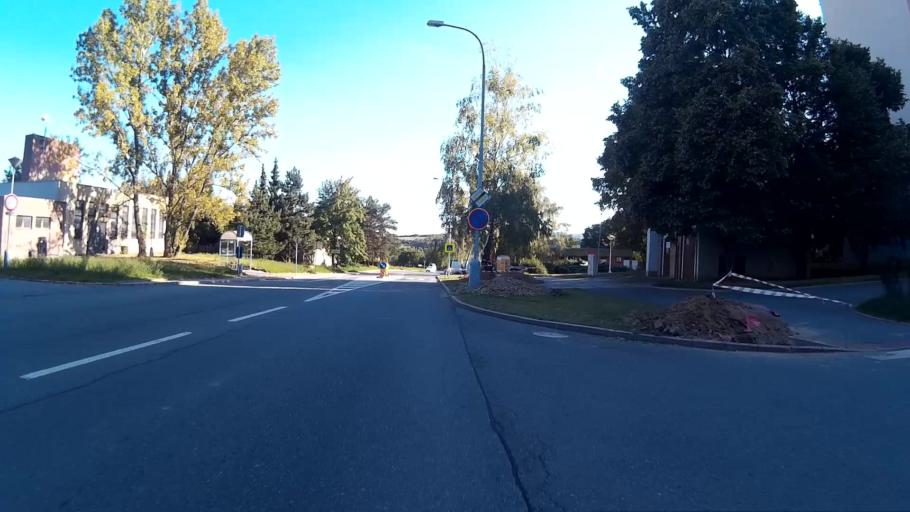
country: CZ
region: South Moravian
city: Moravany
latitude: 49.1672
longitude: 16.5862
